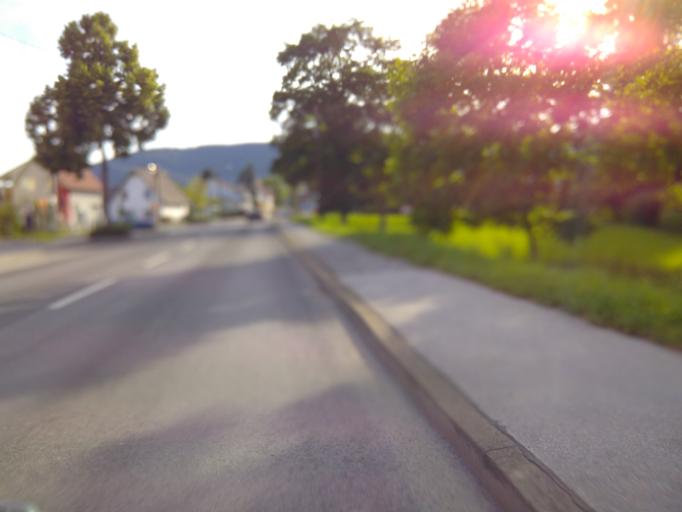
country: AT
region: Styria
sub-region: Graz Stadt
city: Wetzelsdorf
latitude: 47.0525
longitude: 15.4042
